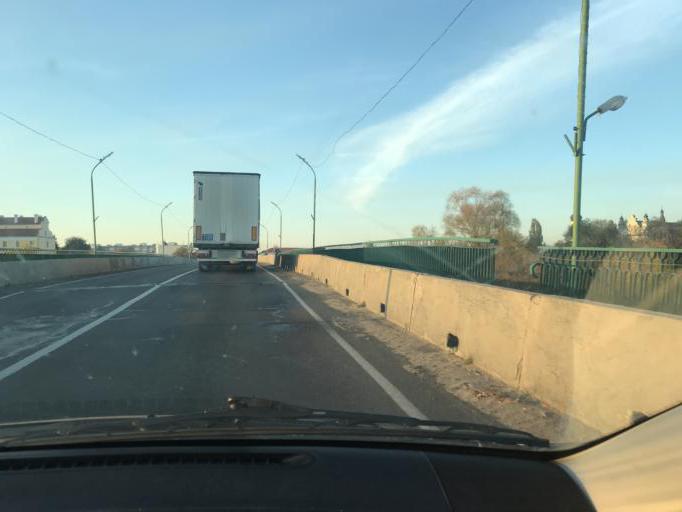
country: BY
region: Brest
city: Pinsk
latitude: 52.1091
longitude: 26.1070
